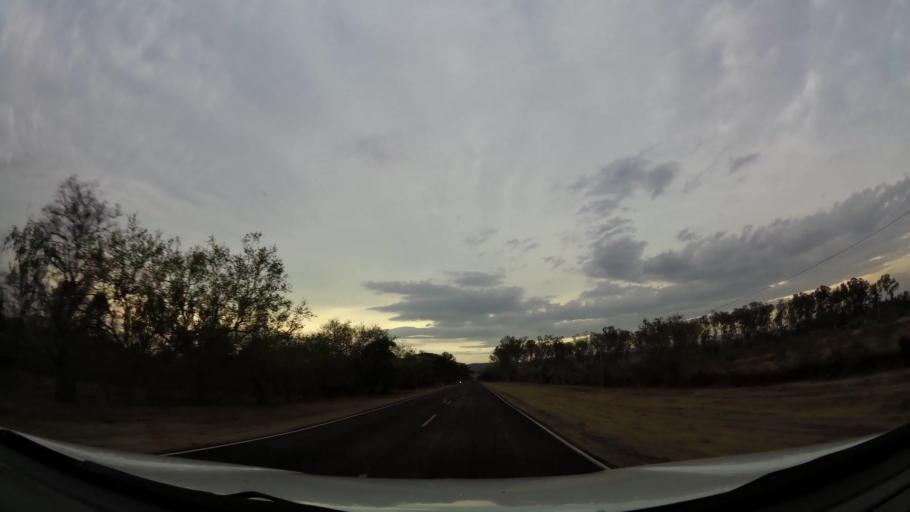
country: NI
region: Matagalpa
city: Ciudad Dario
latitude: 12.8911
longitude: -86.1807
